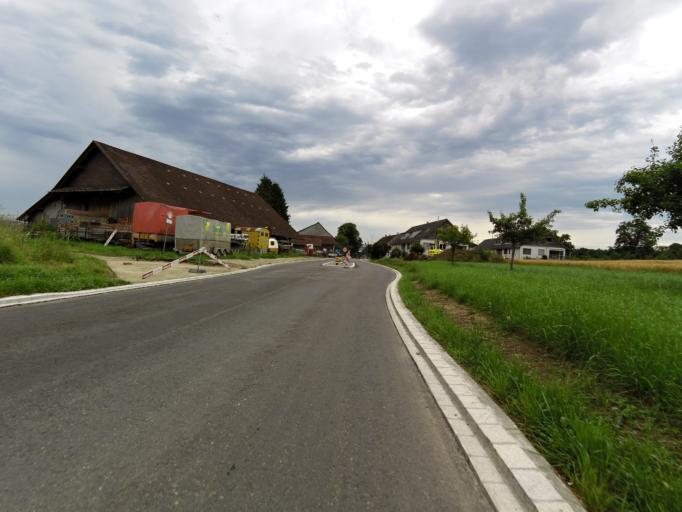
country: CH
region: Thurgau
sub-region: Frauenfeld District
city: Gachnang
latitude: 47.5627
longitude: 8.8661
